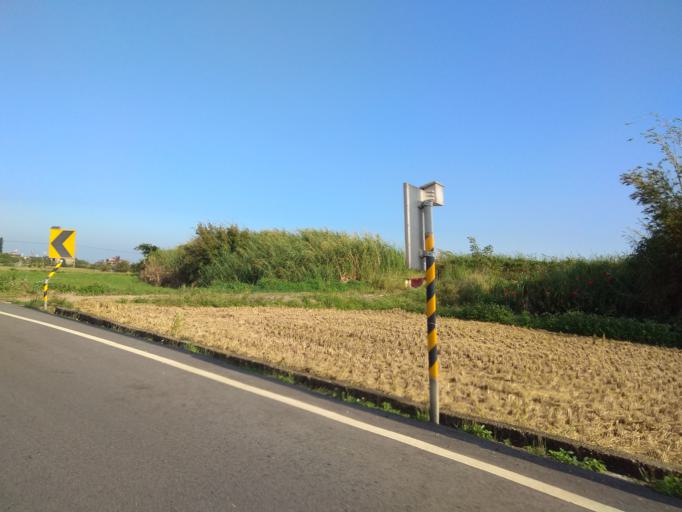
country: TW
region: Taiwan
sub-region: Hsinchu
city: Zhubei
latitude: 24.9928
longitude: 121.0689
